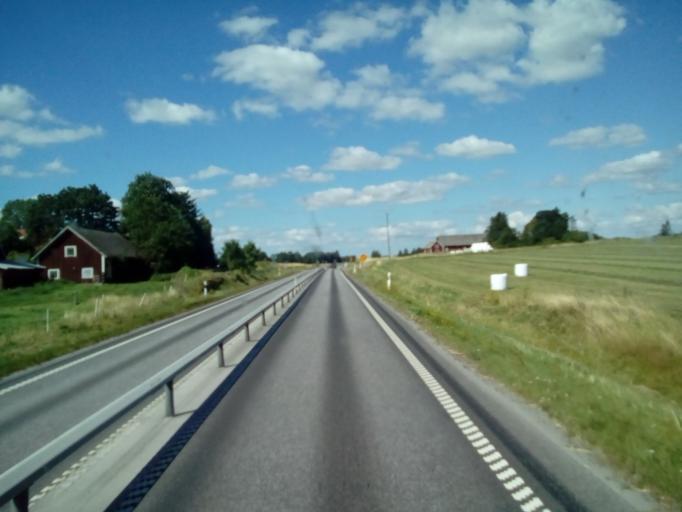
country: SE
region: OEstergoetland
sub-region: Linkopings Kommun
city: Malmslatt
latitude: 58.3336
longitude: 15.5596
